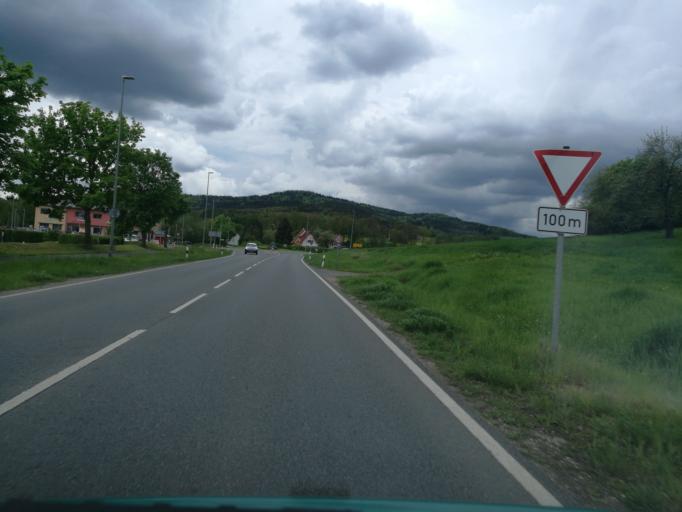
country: DE
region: Bavaria
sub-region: Upper Franconia
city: Altenkunstadt
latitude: 50.1217
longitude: 11.2330
